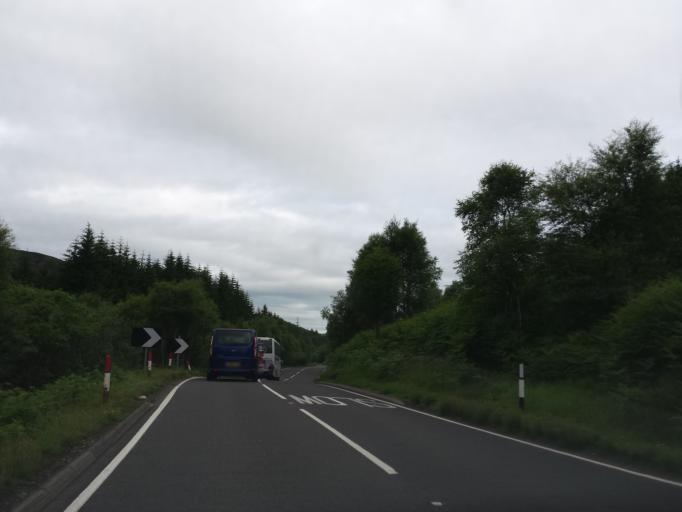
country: GB
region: Scotland
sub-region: Stirling
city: Callander
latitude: 56.4192
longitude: -4.3330
